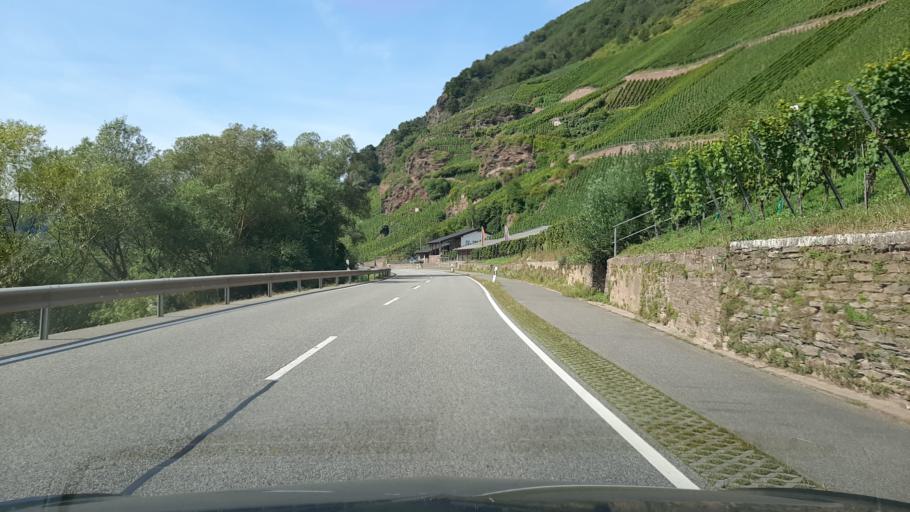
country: DE
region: Rheinland-Pfalz
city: Erden
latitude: 49.9809
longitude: 7.0296
